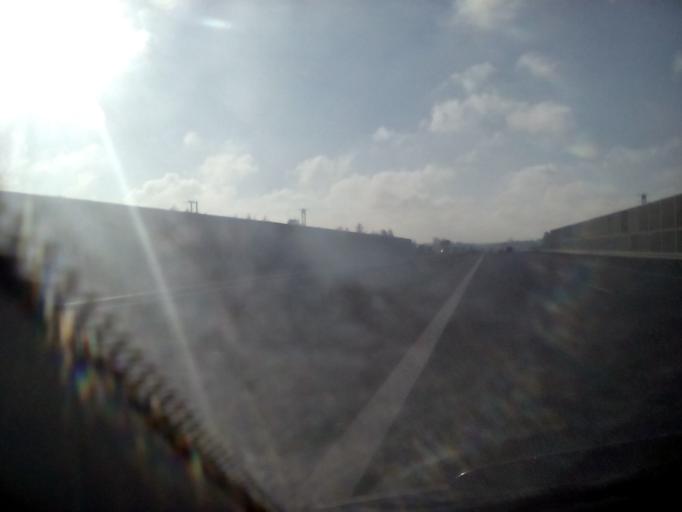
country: PL
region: Masovian Voivodeship
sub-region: Powiat grojecki
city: Grojec
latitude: 51.8132
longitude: 20.8847
